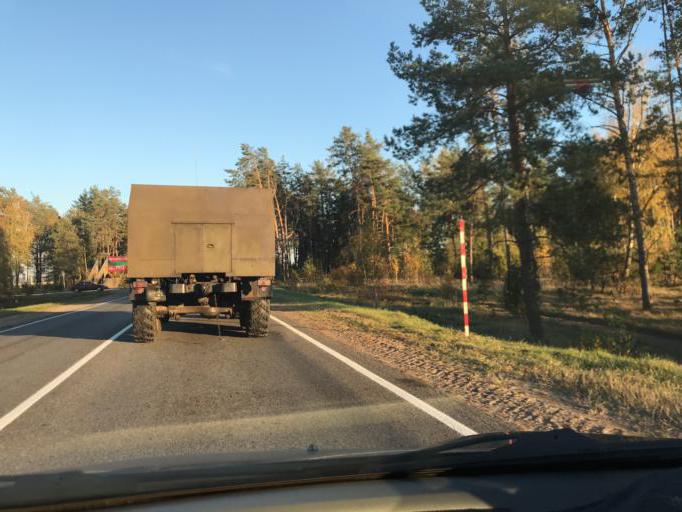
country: BY
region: Minsk
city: Staryya Darohi
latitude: 53.0479
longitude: 28.0862
